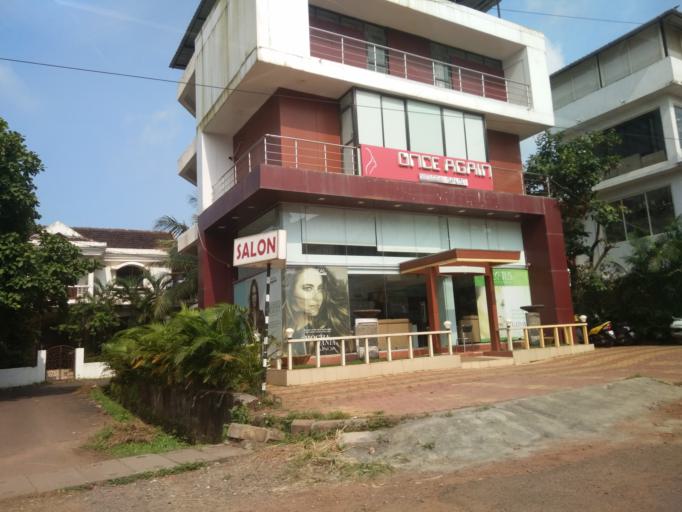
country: IN
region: Goa
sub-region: North Goa
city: Serula
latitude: 15.5346
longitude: 73.8213
